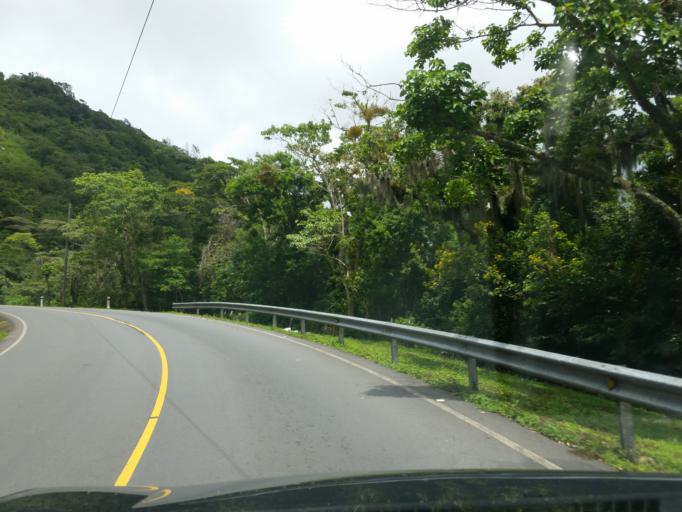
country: NI
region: Matagalpa
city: Matagalpa
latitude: 12.9867
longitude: -85.9208
